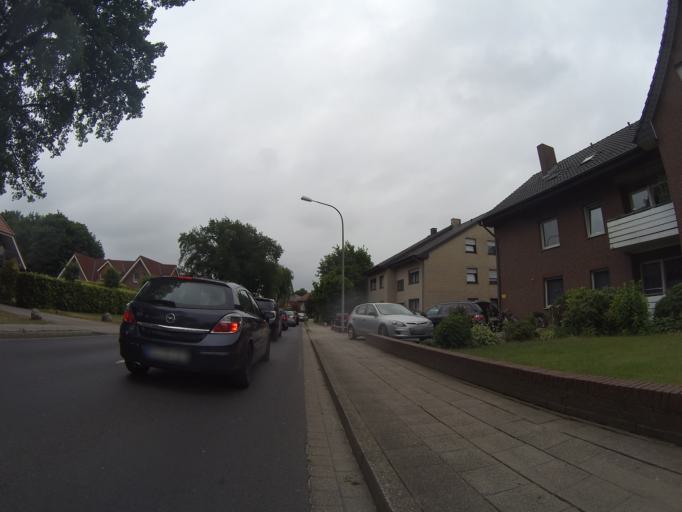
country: DE
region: Lower Saxony
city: Haren
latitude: 52.7891
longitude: 7.2252
